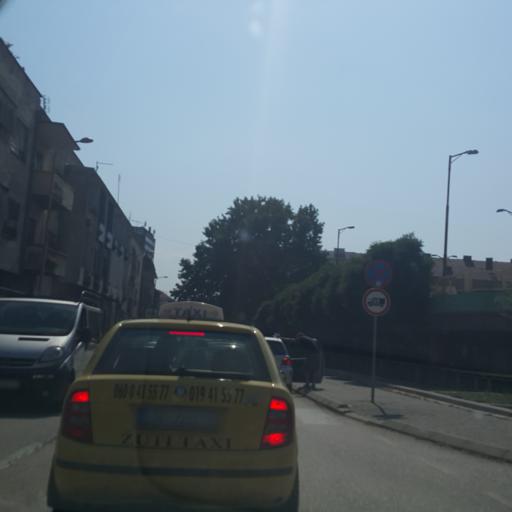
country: RS
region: Central Serbia
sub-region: Zajecarski Okrug
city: Zajecar
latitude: 43.9059
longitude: 22.2783
